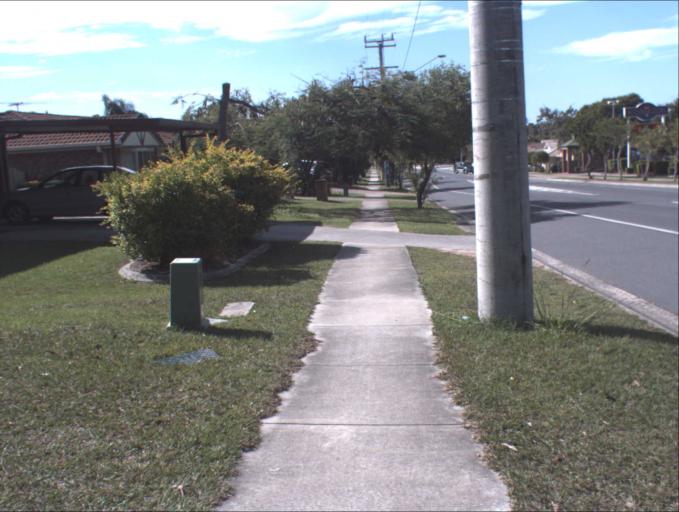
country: AU
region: Queensland
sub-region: Logan
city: Logan Reserve
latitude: -27.6959
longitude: 153.0821
